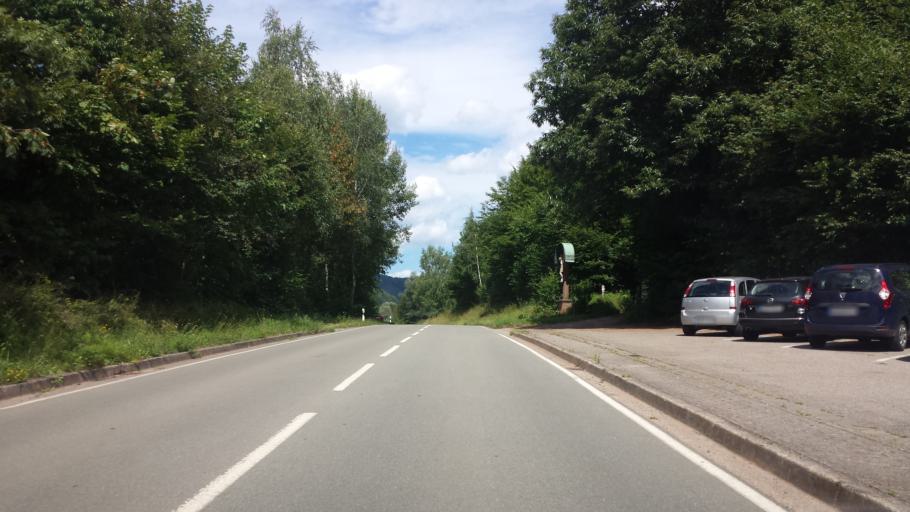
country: DE
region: Rheinland-Pfalz
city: Dernbach
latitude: 49.2509
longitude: 8.0058
